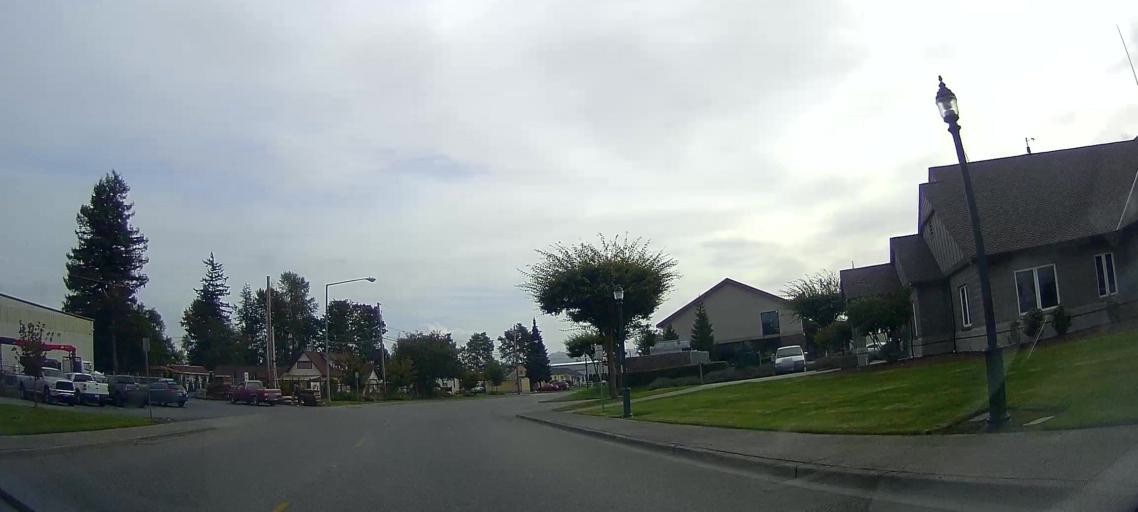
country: US
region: Washington
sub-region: Skagit County
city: Burlington
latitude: 48.4695
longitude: -122.3306
